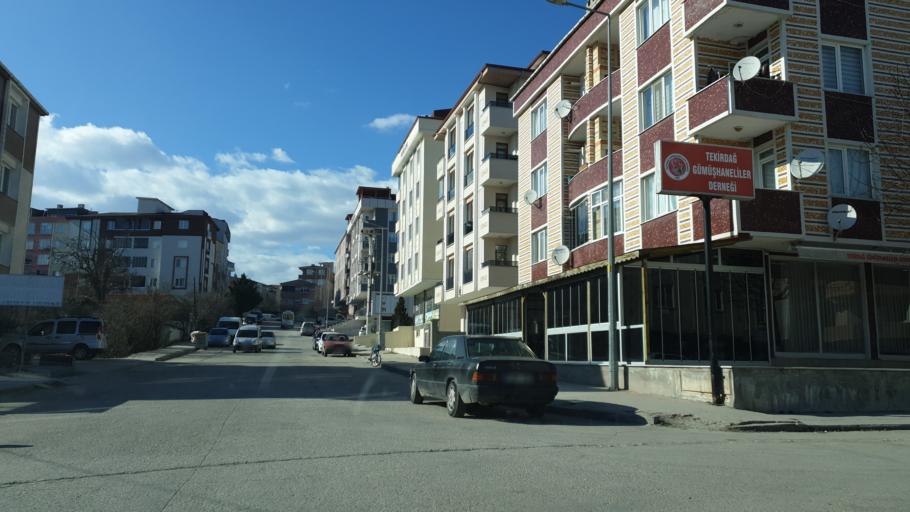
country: TR
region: Tekirdag
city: Cerkezkoey
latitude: 41.2880
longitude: 28.0057
